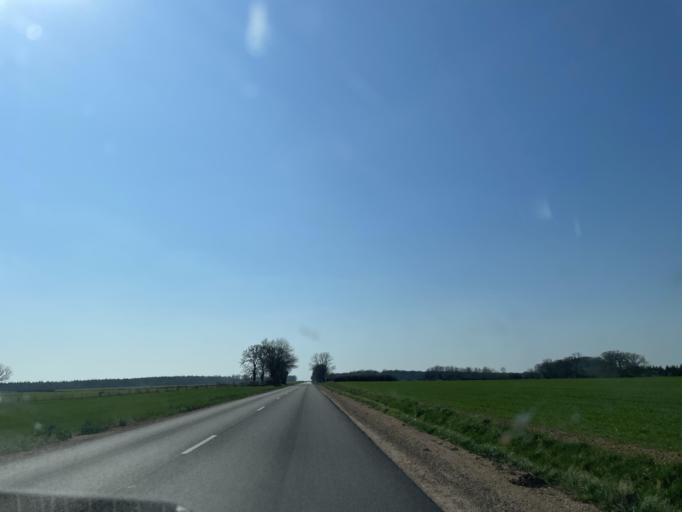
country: FR
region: Bourgogne
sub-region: Departement de la Cote-d'Or
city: Semur-en-Auxois
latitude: 47.4561
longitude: 4.3397
